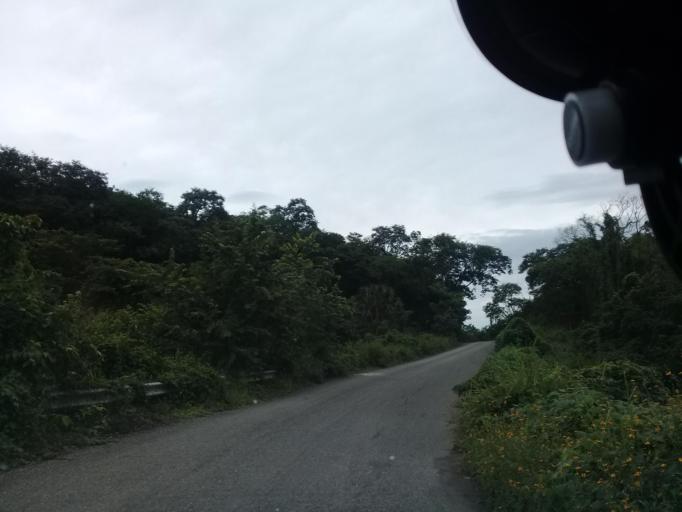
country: MX
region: Hidalgo
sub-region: Huejutla de Reyes
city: Chalahuiyapa
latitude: 21.1997
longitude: -98.3495
